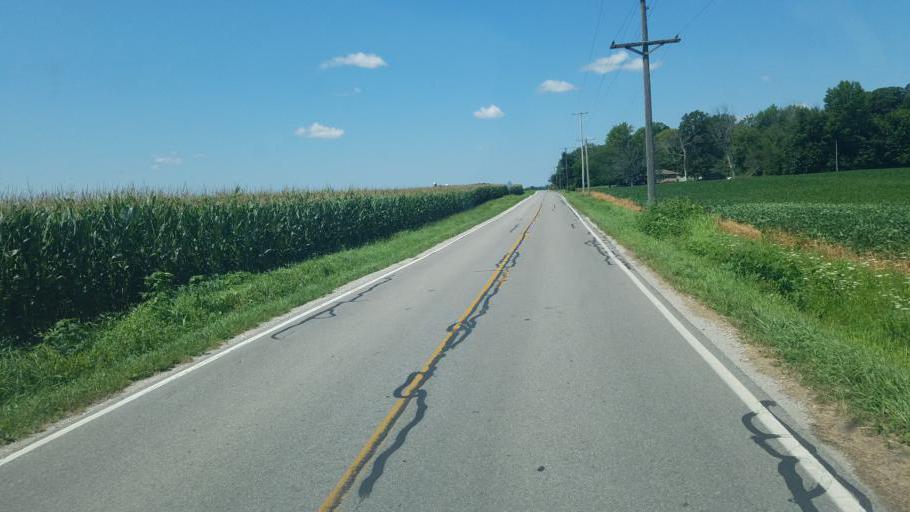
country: US
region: Ohio
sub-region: Marion County
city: Prospect
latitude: 40.4839
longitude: -83.1525
